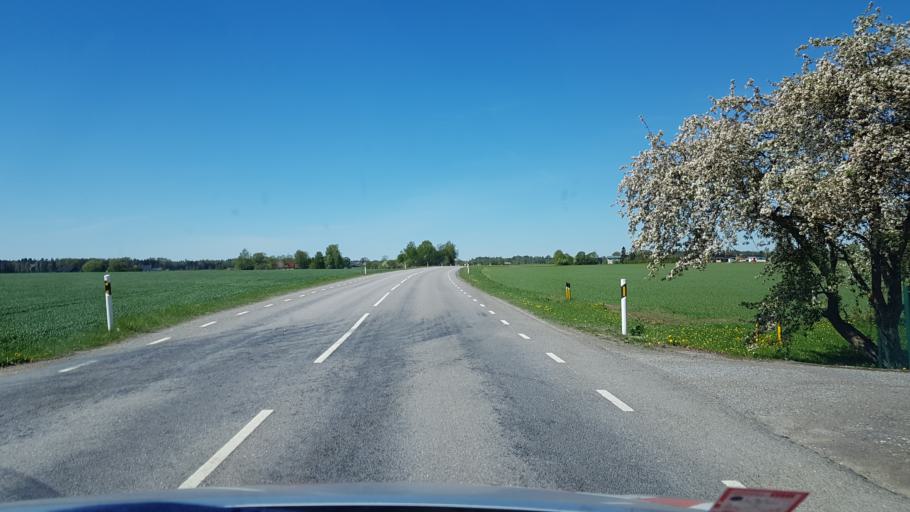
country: EE
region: Tartu
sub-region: Tartu linn
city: Tartu
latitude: 58.3794
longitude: 26.6654
